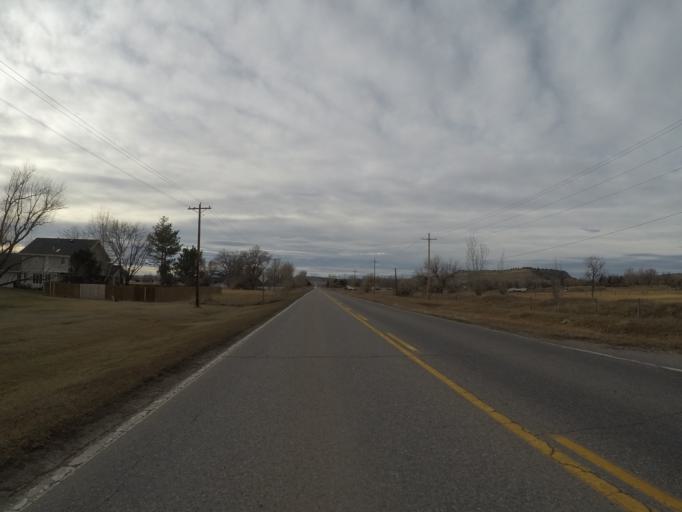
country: US
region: Montana
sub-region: Yellowstone County
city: Billings
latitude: 45.7987
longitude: -108.6566
